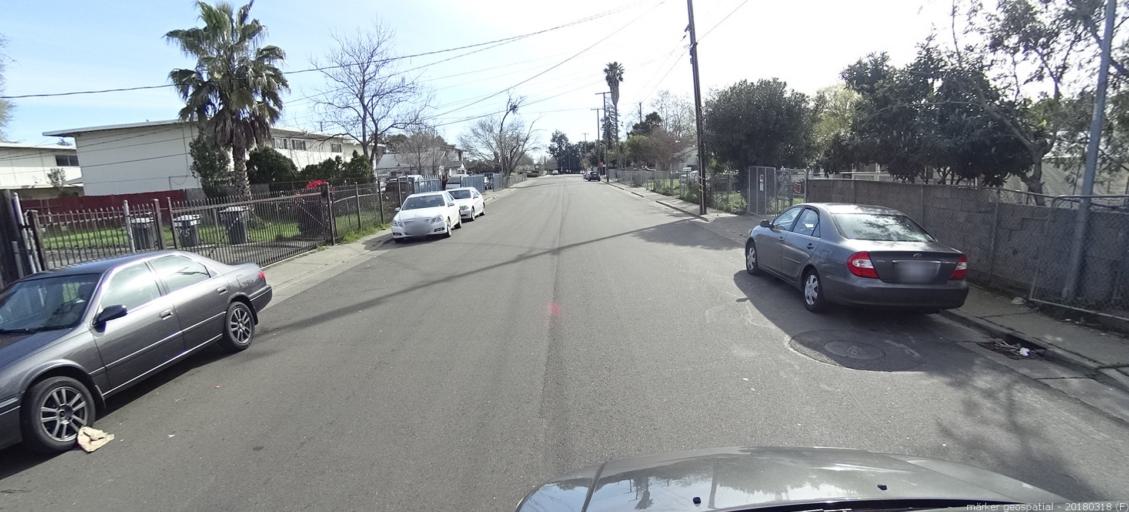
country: US
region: California
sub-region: Sacramento County
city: Parkway
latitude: 38.5151
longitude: -121.4660
